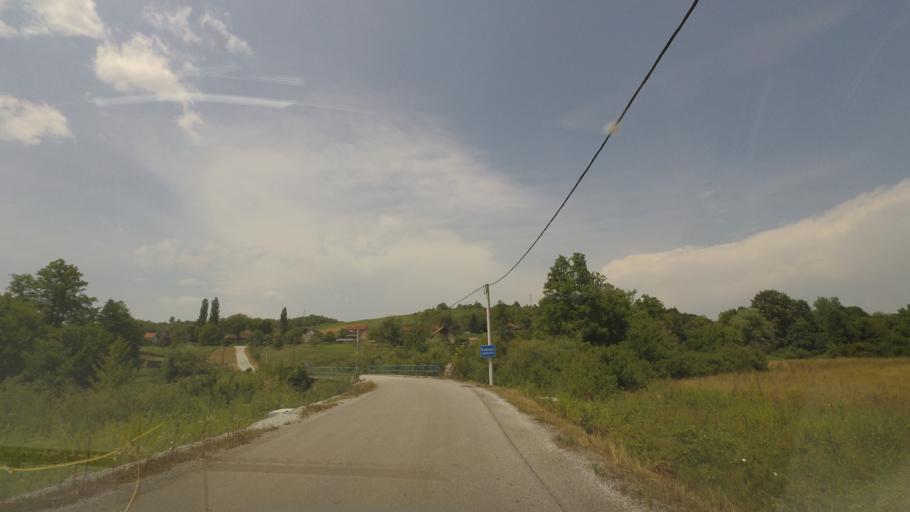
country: HR
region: Karlovacka
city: Vojnic
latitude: 45.3815
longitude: 15.6099
